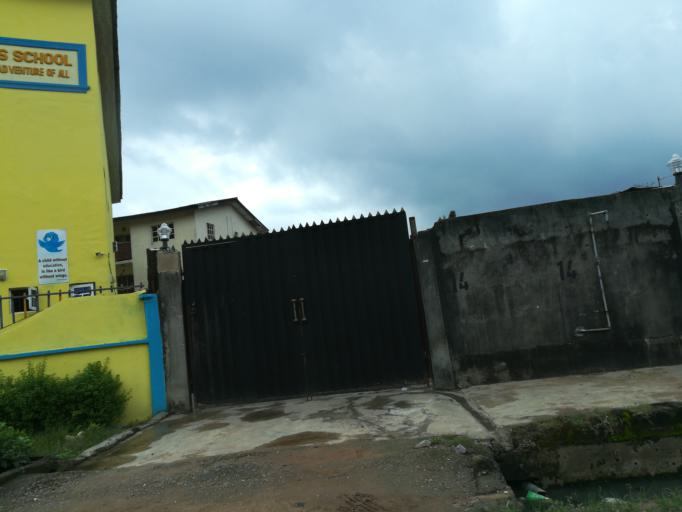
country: NG
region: Lagos
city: Agege
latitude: 6.6065
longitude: 3.3078
